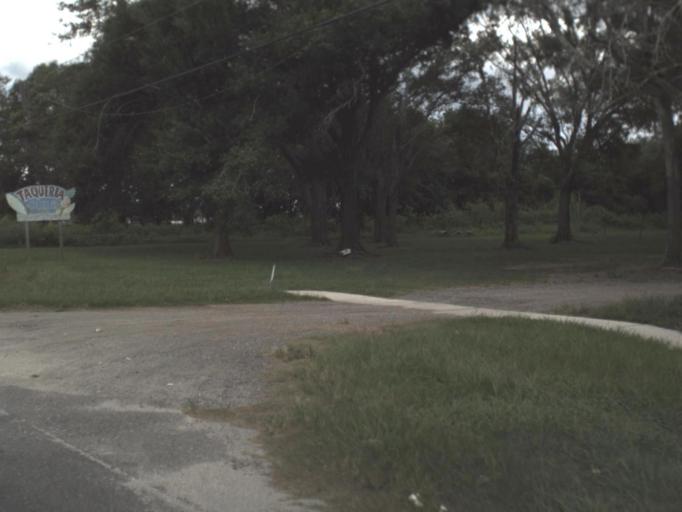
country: US
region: Florida
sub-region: Hillsborough County
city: Sun City Center
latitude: 27.7125
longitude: -82.3266
